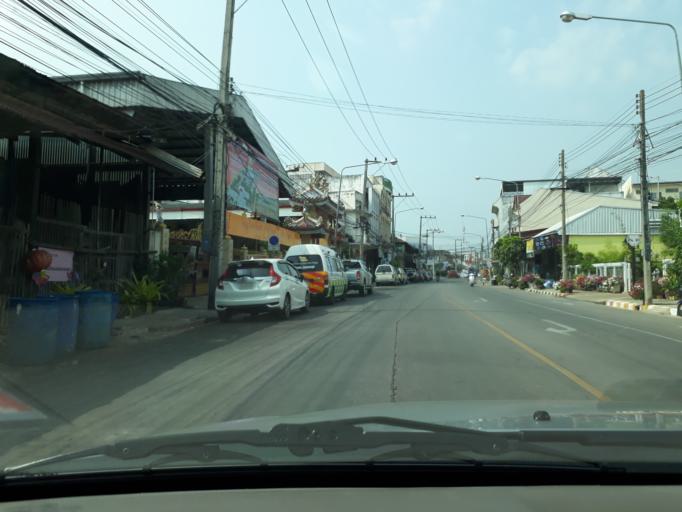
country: TH
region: Khon Kaen
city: Khon Kaen
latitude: 16.4288
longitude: 102.8375
